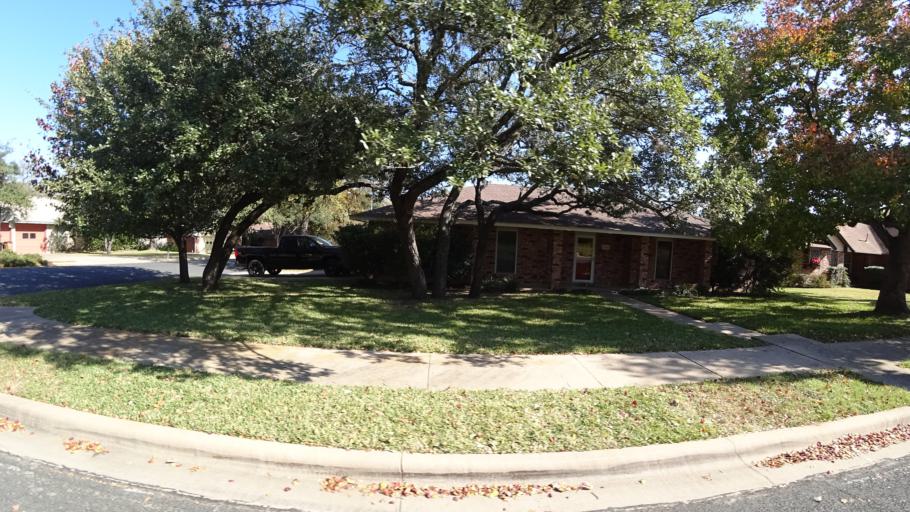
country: US
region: Texas
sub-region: Travis County
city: Shady Hollow
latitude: 30.2221
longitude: -97.8591
